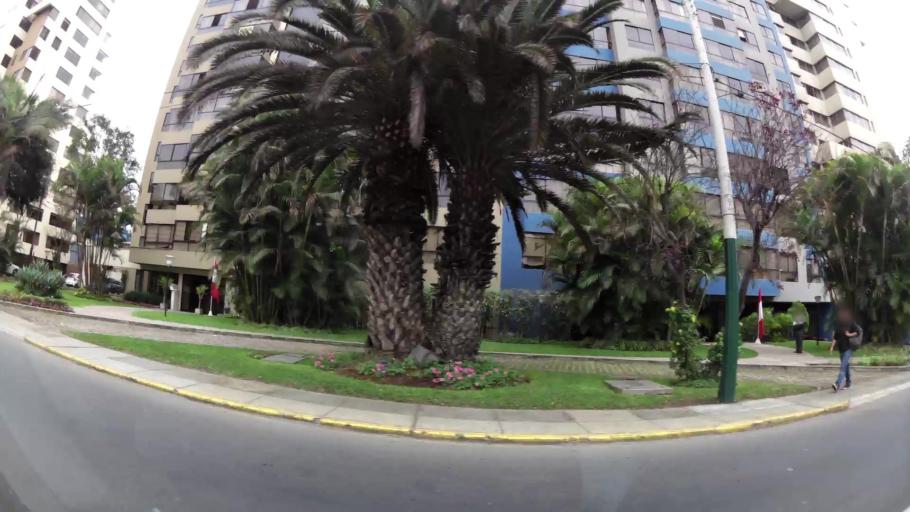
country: PE
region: Lima
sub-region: Lima
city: San Isidro
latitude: -12.0933
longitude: -77.0398
